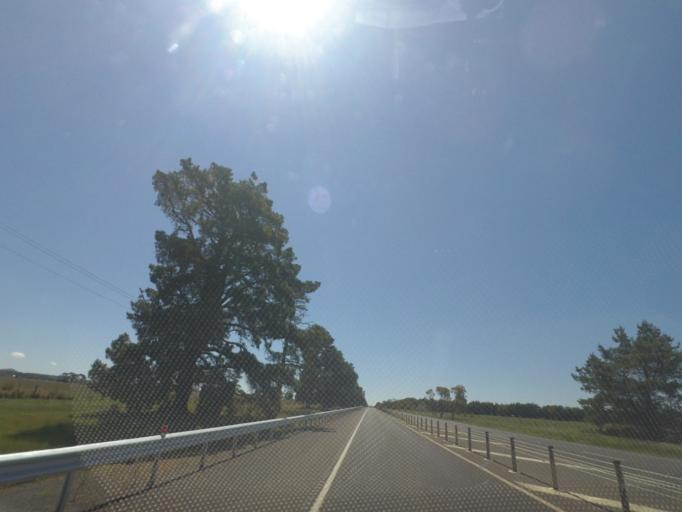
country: AU
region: Victoria
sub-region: Hume
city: Sunbury
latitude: -37.3808
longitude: 144.7466
